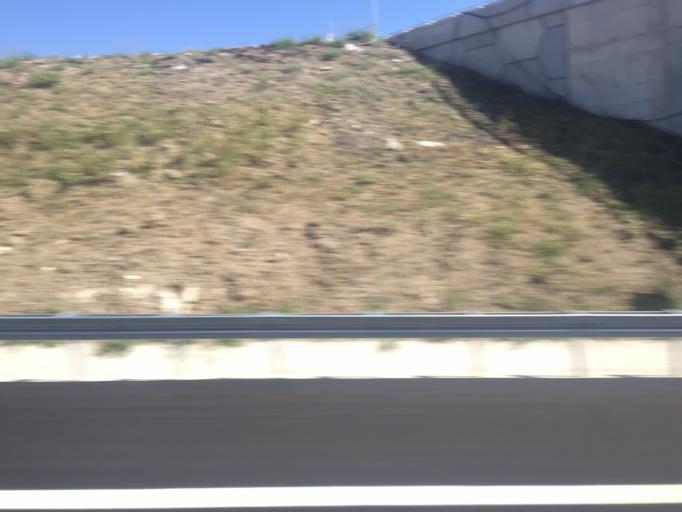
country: TR
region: Bursa
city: Gorukle
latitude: 40.2440
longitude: 28.7634
